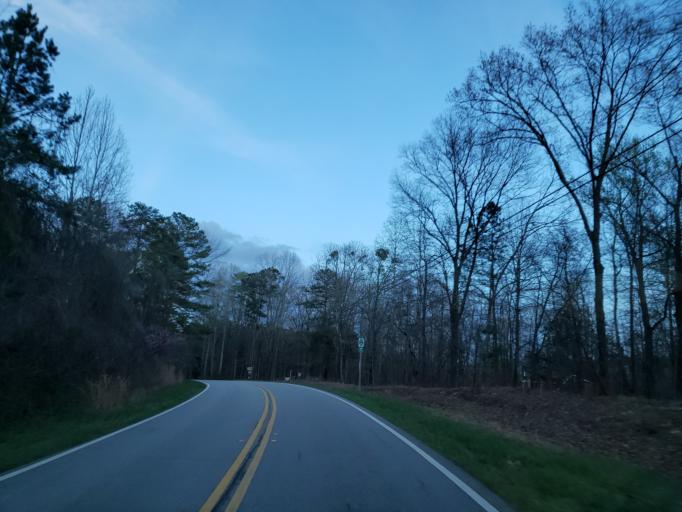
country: US
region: Georgia
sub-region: Polk County
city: Rockmart
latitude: 33.9891
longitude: -84.9547
